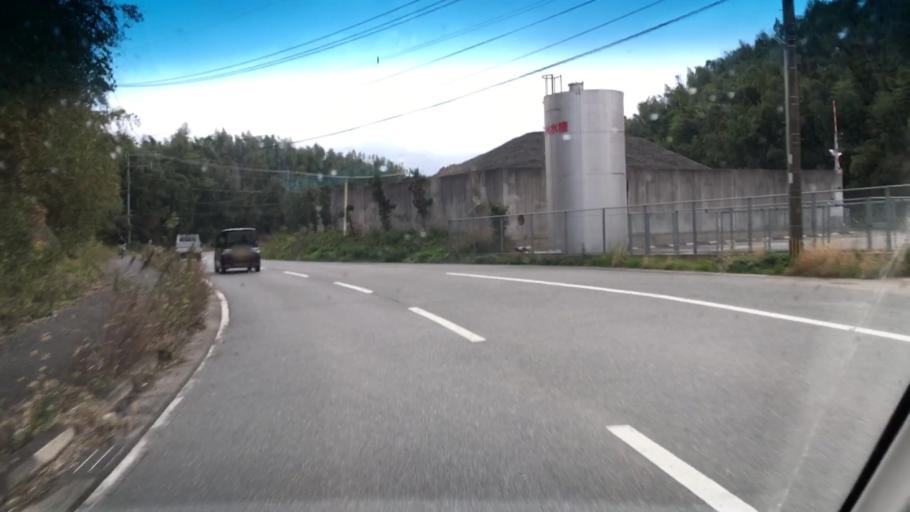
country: JP
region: Fukuoka
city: Maebaru-chuo
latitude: 33.5305
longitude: 130.1968
